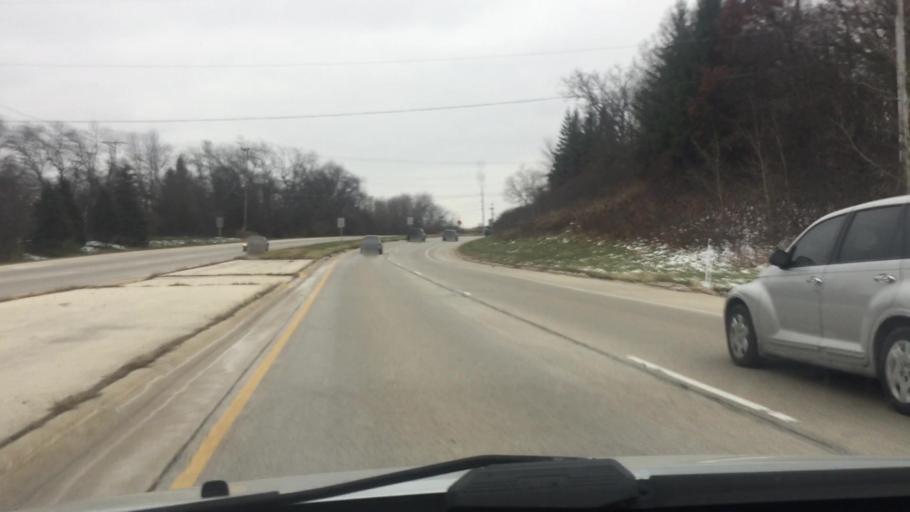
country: US
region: Wisconsin
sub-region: Waukesha County
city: Delafield
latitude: 43.0577
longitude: -88.3690
